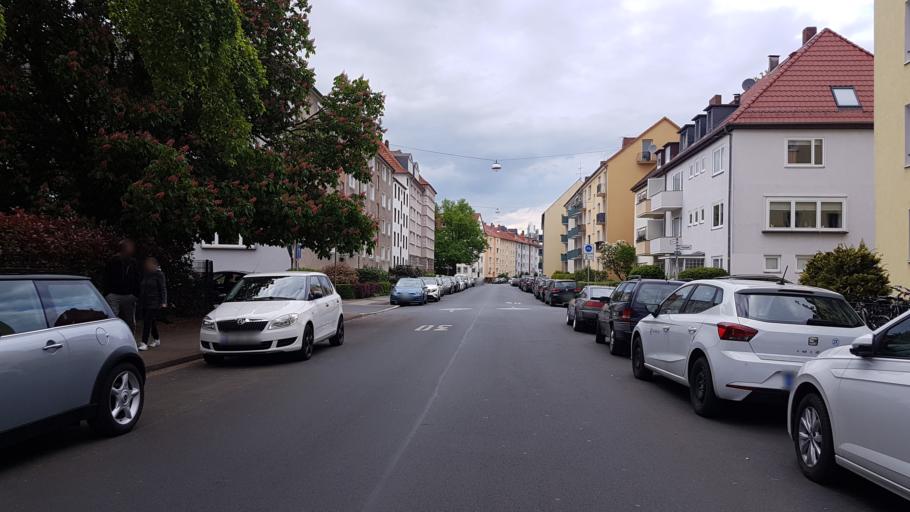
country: DE
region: Lower Saxony
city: Hannover
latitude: 52.3588
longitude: 9.7477
